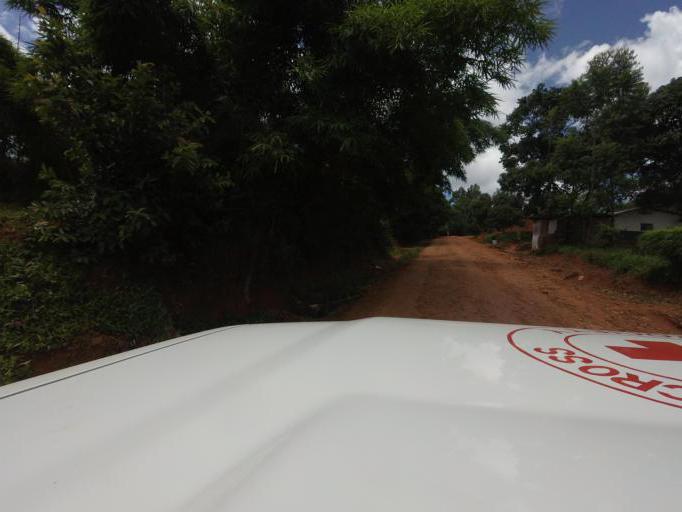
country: MW
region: Southern Region
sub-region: Thyolo District
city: Thyolo
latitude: -16.0363
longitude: 35.0553
